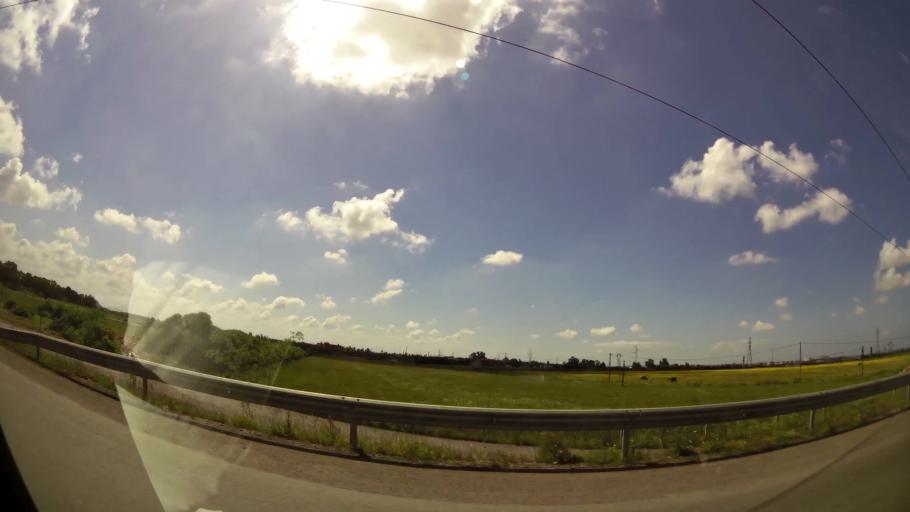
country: MA
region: Grand Casablanca
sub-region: Nouaceur
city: Bouskoura
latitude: 33.5068
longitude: -7.6113
